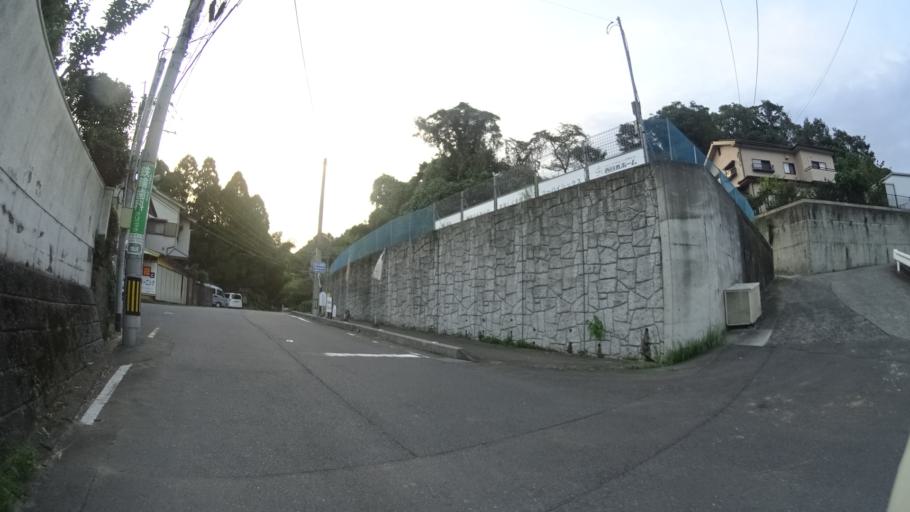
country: JP
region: Oita
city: Beppu
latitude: 33.3189
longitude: 131.4845
